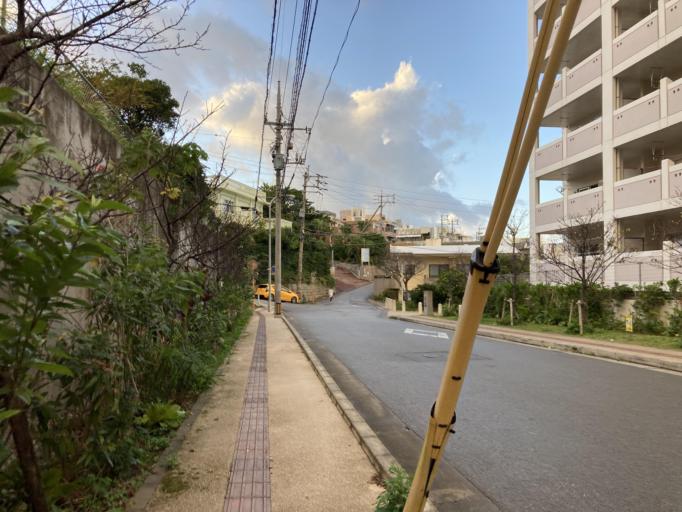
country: JP
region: Okinawa
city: Naha-shi
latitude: 26.2226
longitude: 127.7245
